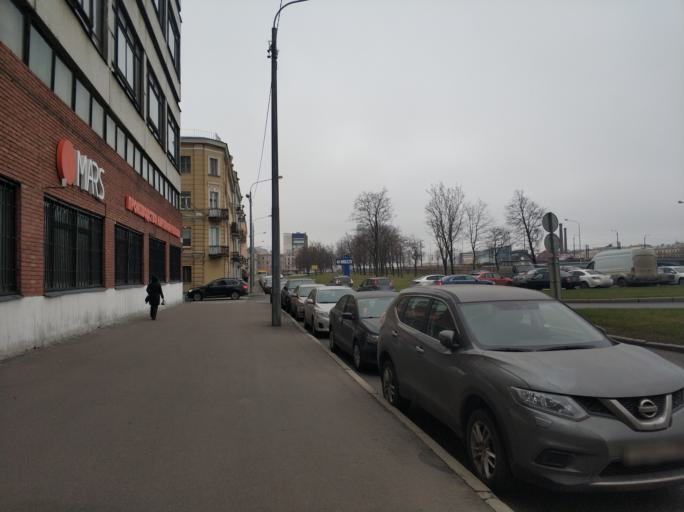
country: RU
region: Leningrad
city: Sampsonievskiy
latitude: 59.9704
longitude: 30.3365
